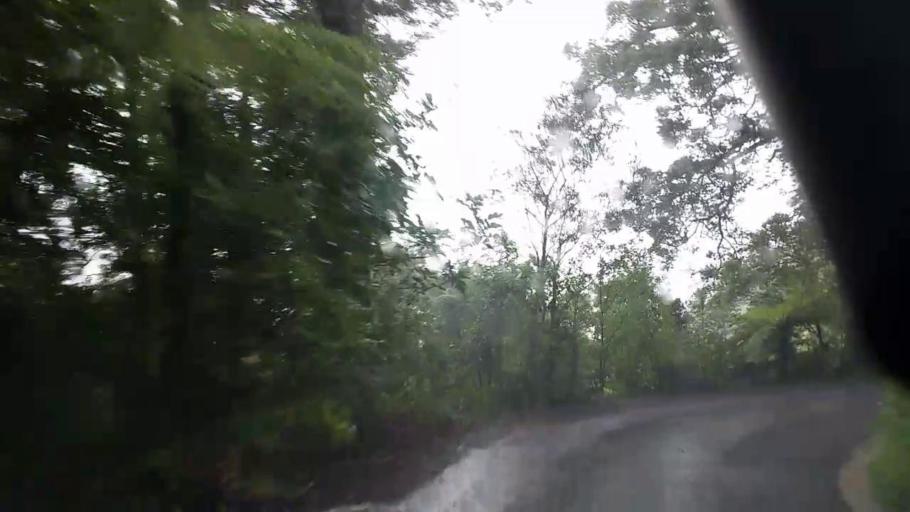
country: NZ
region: Auckland
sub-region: Auckland
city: Waitakere
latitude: -36.9167
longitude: 174.5648
